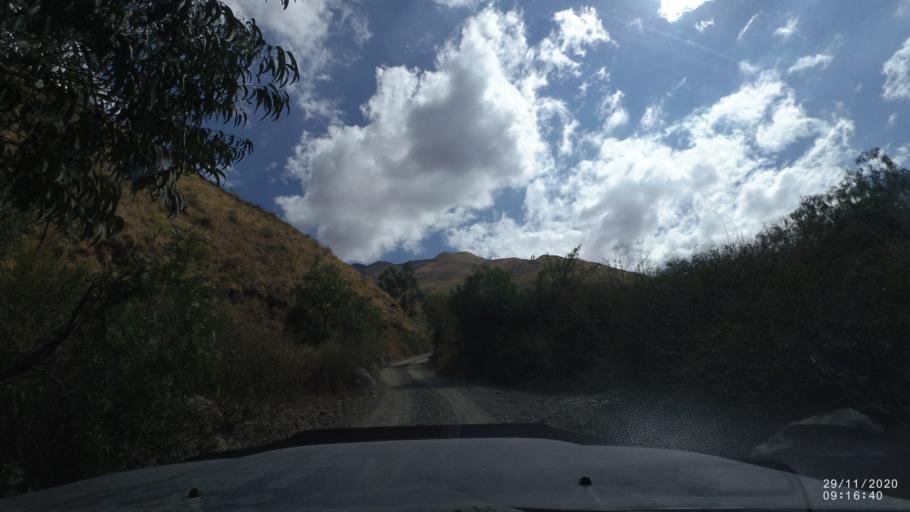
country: BO
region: Cochabamba
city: Cochabamba
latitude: -17.3262
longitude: -66.1857
